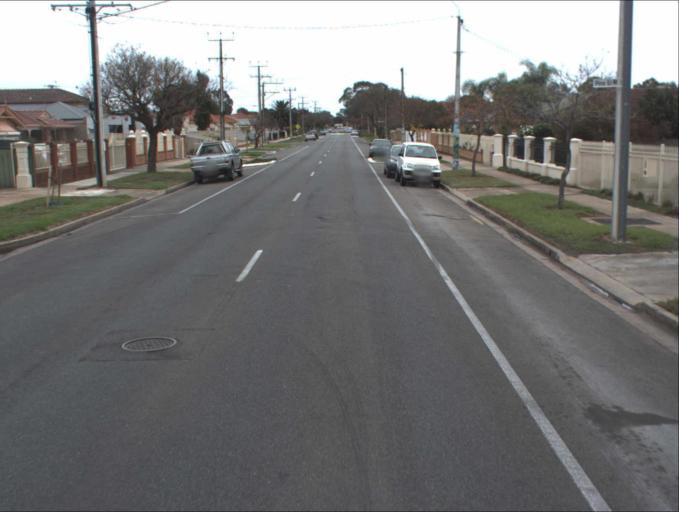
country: AU
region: South Australia
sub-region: Charles Sturt
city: Woodville North
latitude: -34.8639
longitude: 138.5549
